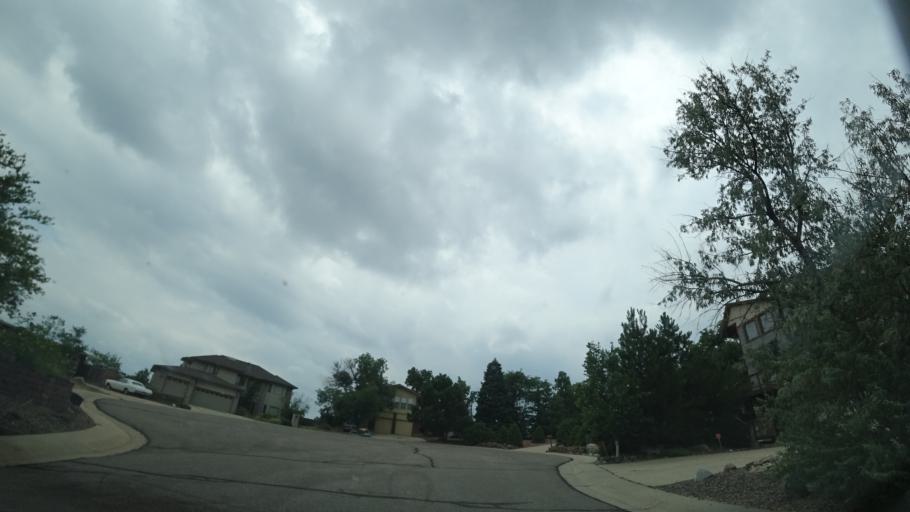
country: US
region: Colorado
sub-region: Jefferson County
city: West Pleasant View
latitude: 39.7047
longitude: -105.1566
